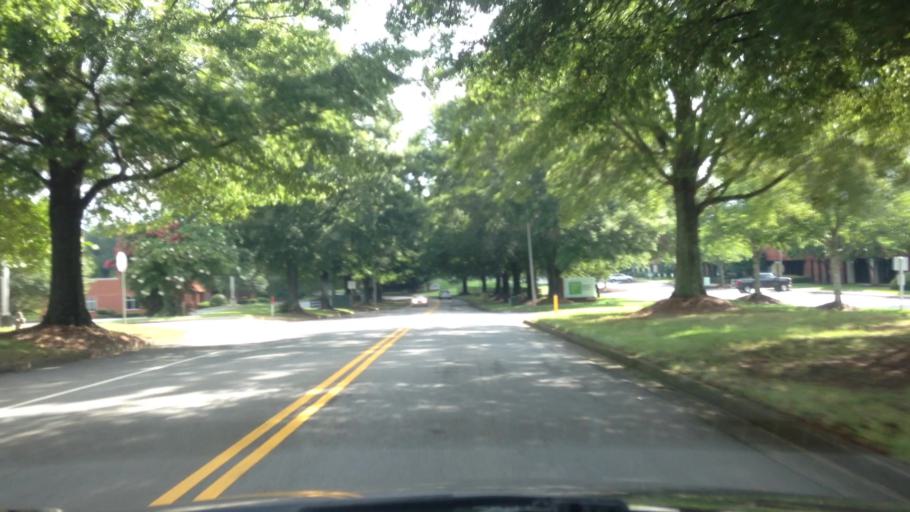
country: US
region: Georgia
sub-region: Fulton County
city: Johns Creek
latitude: 34.1111
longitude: -84.2033
